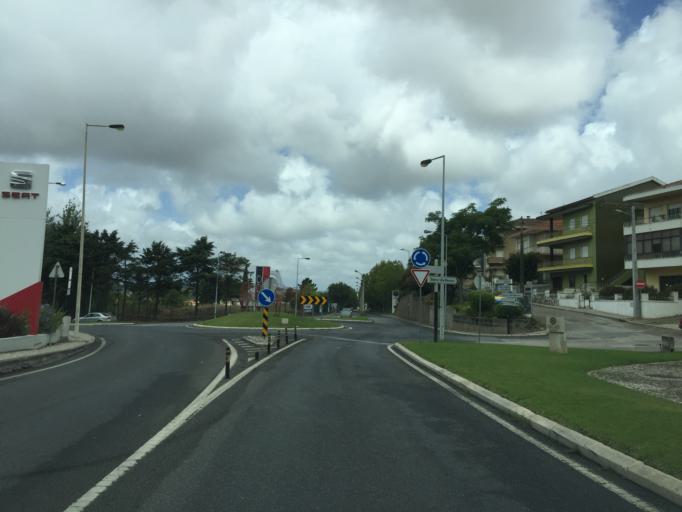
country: PT
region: Lisbon
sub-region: Torres Vedras
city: Torres Vedras
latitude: 39.0811
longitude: -9.2553
